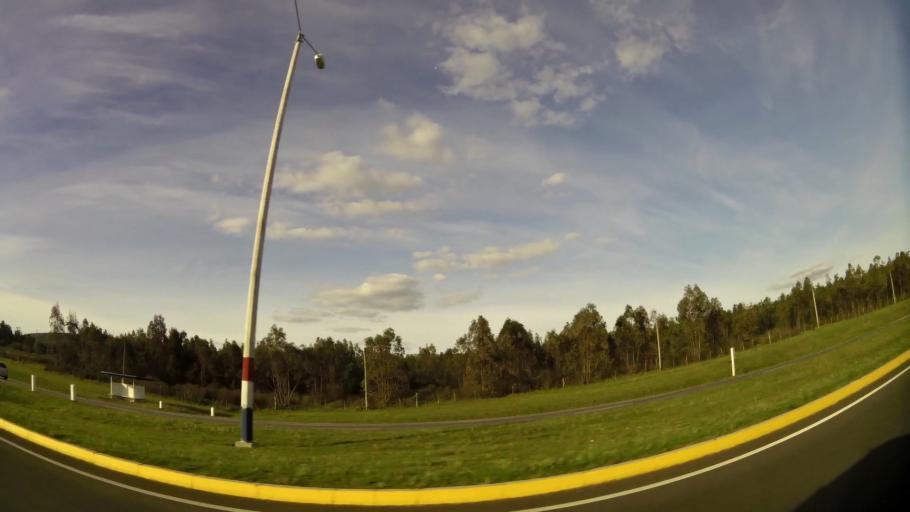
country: UY
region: Maldonado
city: Pan de Azucar
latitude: -34.7891
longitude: -55.3217
